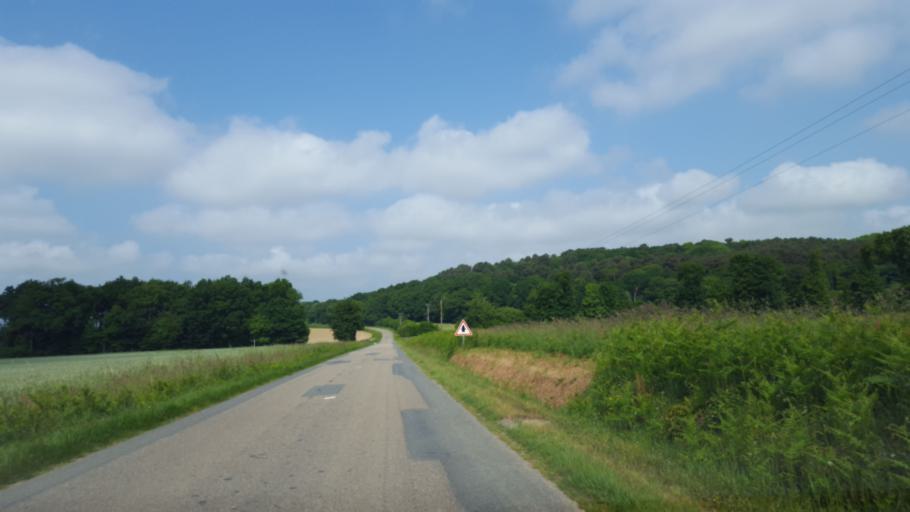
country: FR
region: Brittany
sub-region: Departement d'Ille-et-Vilaine
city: Guignen
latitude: 47.9260
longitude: -1.8919
